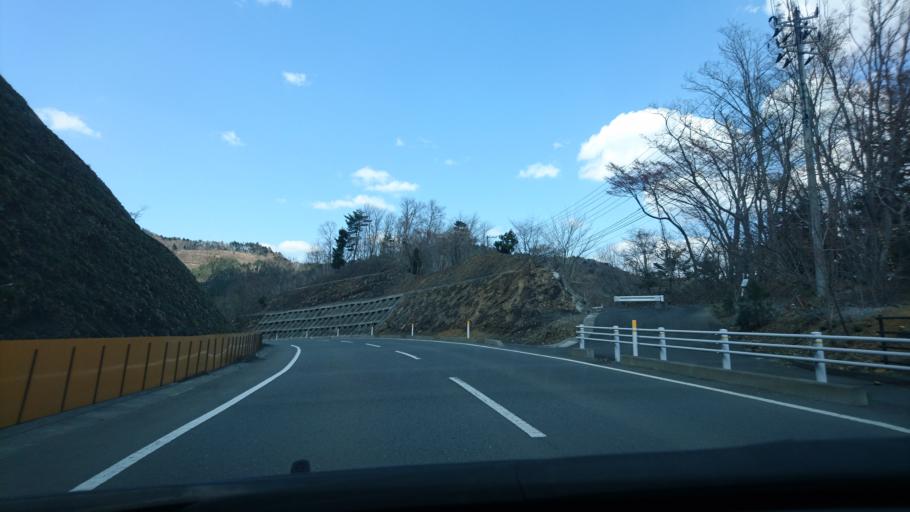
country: JP
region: Miyagi
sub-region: Oshika Gun
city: Onagawa Cho
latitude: 38.4858
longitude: 141.4918
